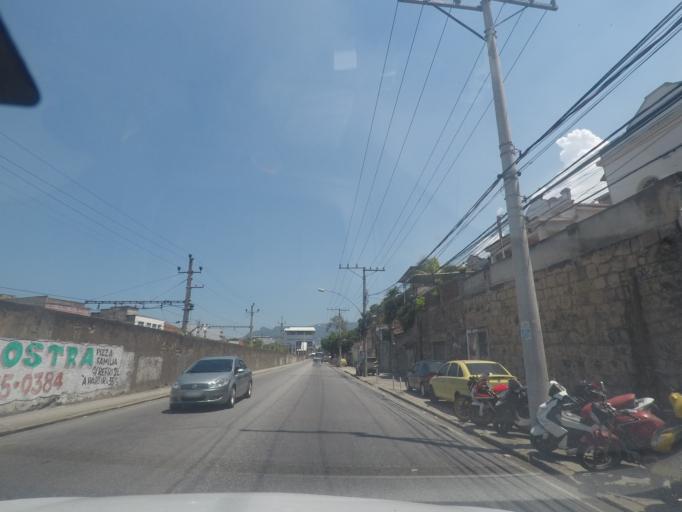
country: BR
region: Rio de Janeiro
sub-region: Rio De Janeiro
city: Rio de Janeiro
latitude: -22.8642
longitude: -43.2567
